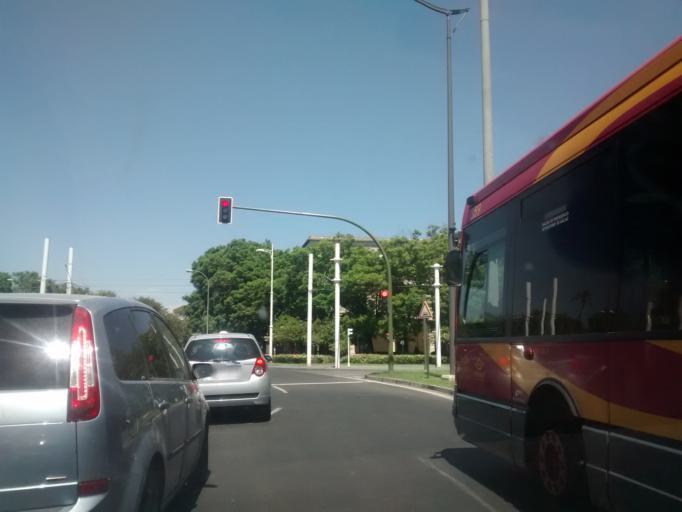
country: ES
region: Andalusia
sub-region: Provincia de Sevilla
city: Sevilla
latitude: 37.3810
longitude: -5.9884
